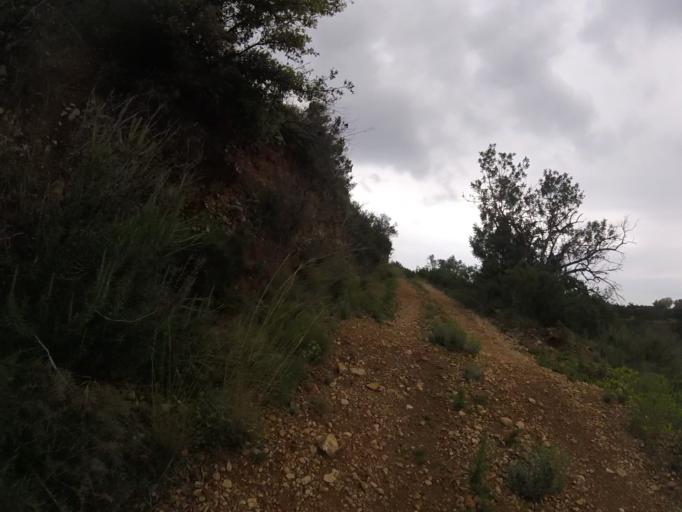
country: ES
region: Valencia
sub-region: Provincia de Castello
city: Cuevas de Vinroma
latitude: 40.2930
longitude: 0.0863
